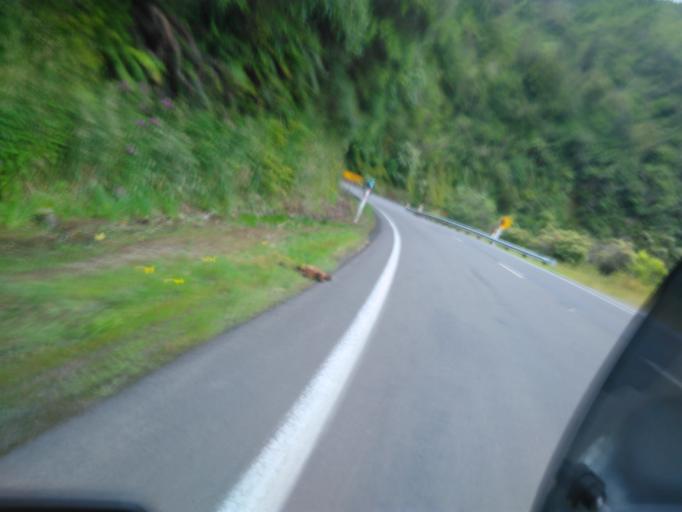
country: NZ
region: Bay of Plenty
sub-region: Opotiki District
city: Opotiki
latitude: -38.2403
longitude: 177.3096
